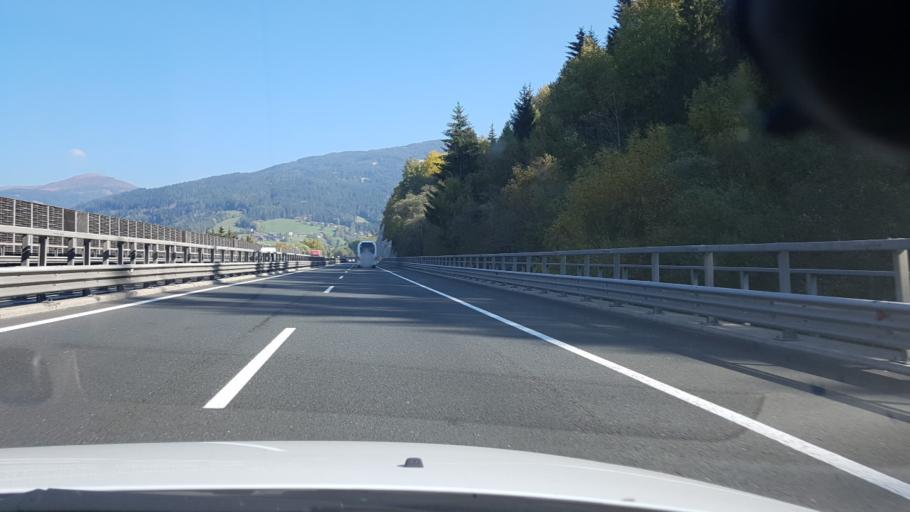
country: AT
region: Carinthia
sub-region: Politischer Bezirk Spittal an der Drau
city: Gmuend
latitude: 46.9285
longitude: 13.5923
